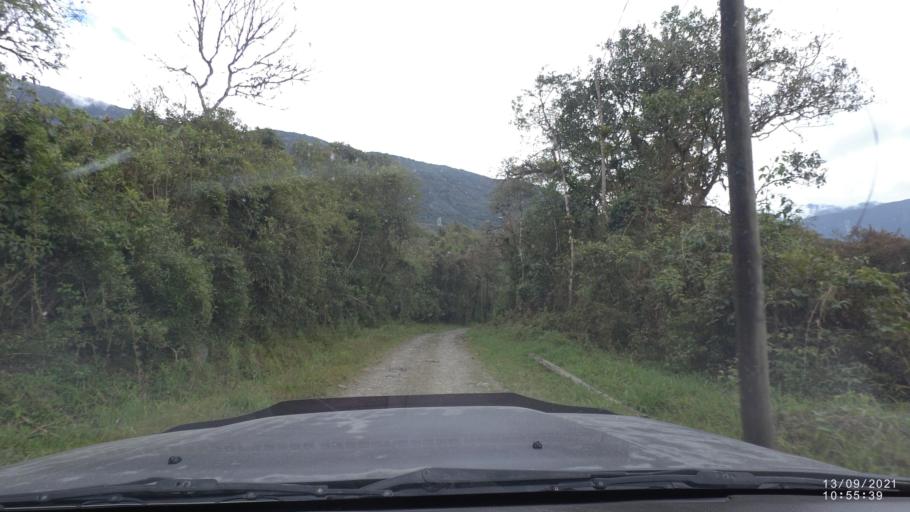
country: BO
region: Cochabamba
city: Colomi
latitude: -17.2147
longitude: -65.8246
